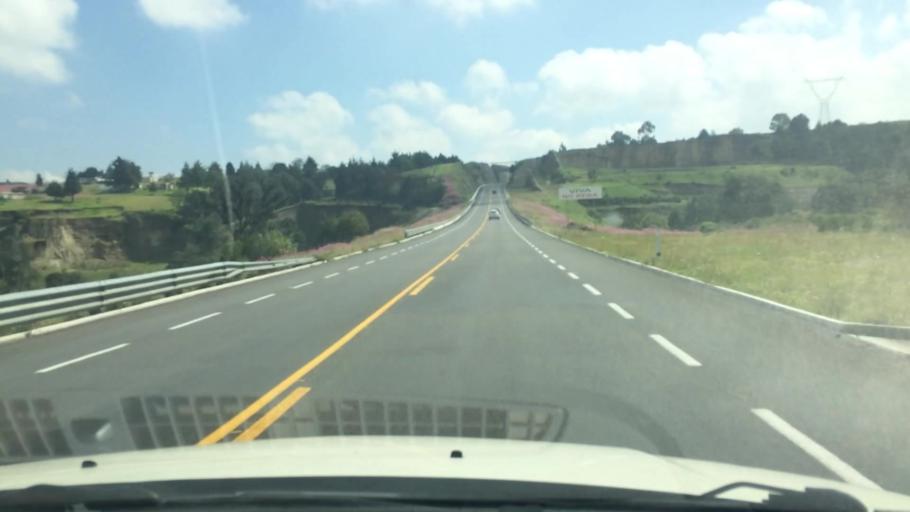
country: MX
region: Mexico
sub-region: Almoloya de Juarez
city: San Pedro de la Hortaliza (Ejido Almoloyan)
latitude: 19.3773
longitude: -99.8664
